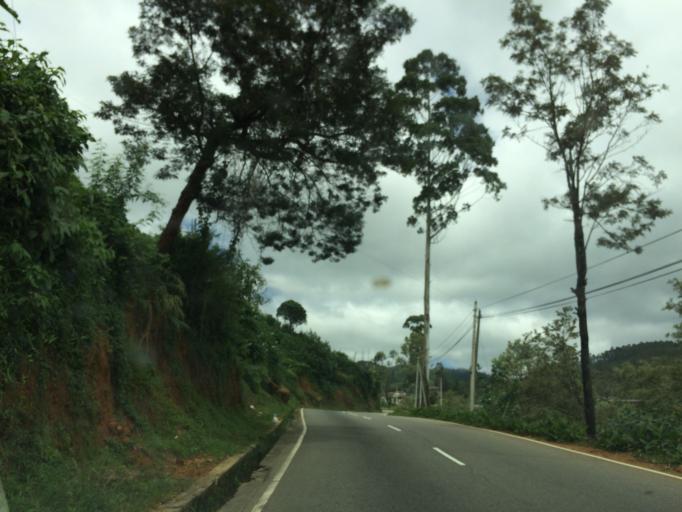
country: LK
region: Central
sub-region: Nuwara Eliya District
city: Nuwara Eliya
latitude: 7.0228
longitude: 80.7218
